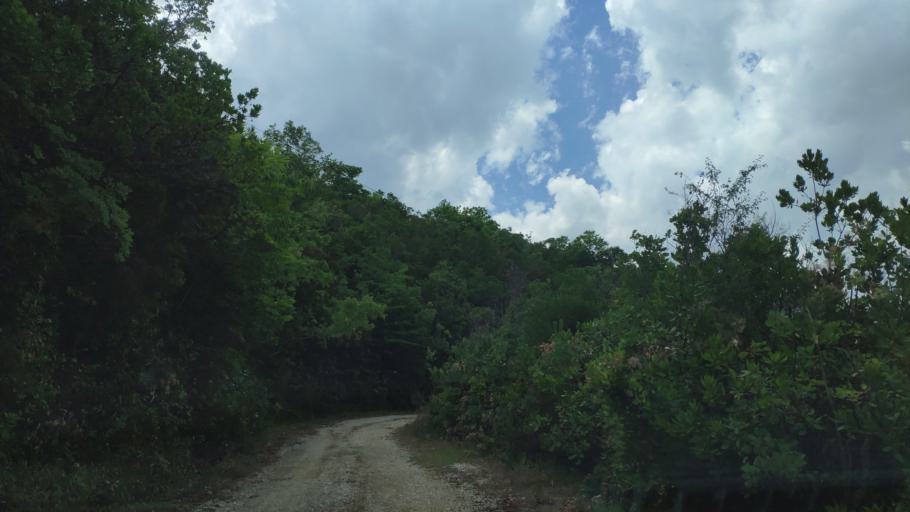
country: GR
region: Epirus
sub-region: Nomos Artas
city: Agios Dimitrios
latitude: 39.3143
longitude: 21.0180
